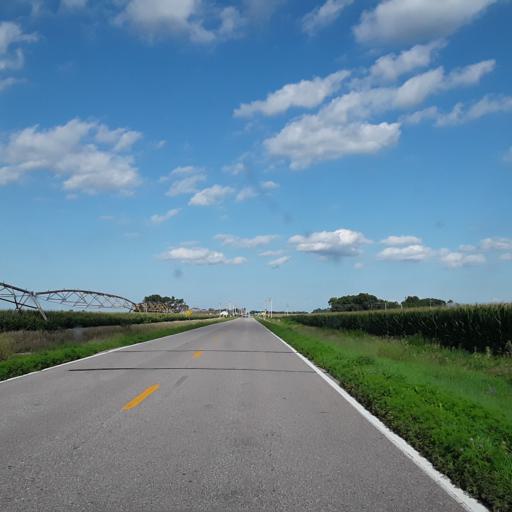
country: US
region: Nebraska
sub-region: Hall County
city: Wood River
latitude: 40.8877
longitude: -98.6132
